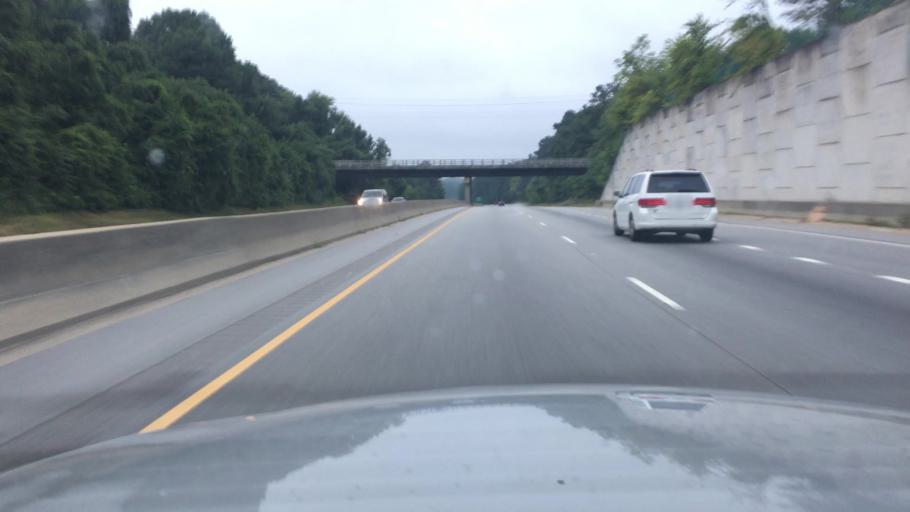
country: US
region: North Carolina
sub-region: Cumberland County
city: Fayetteville
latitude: 35.0539
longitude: -78.8939
